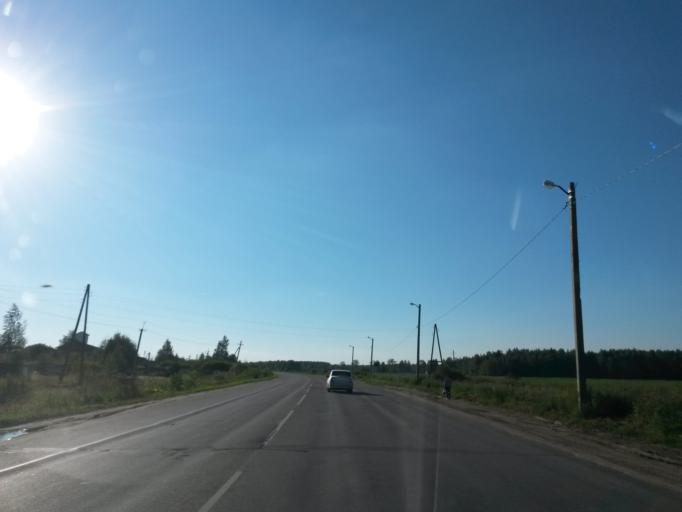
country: RU
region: Ivanovo
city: Novo-Talitsy
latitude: 57.0104
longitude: 40.8363
